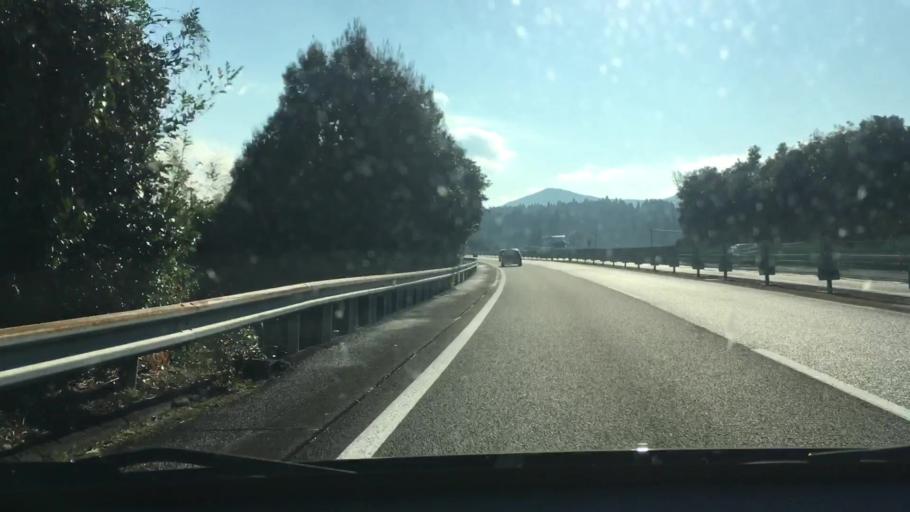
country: JP
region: Kagoshima
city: Okuchi-shinohara
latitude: 32.0119
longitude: 130.7577
